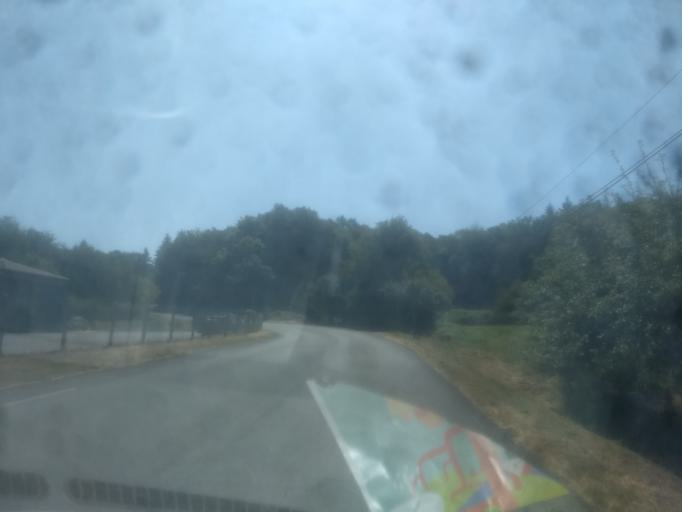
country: FR
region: Limousin
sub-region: Departement de la Haute-Vienne
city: Bessines-sur-Gartempe
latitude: 46.1048
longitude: 1.3729
